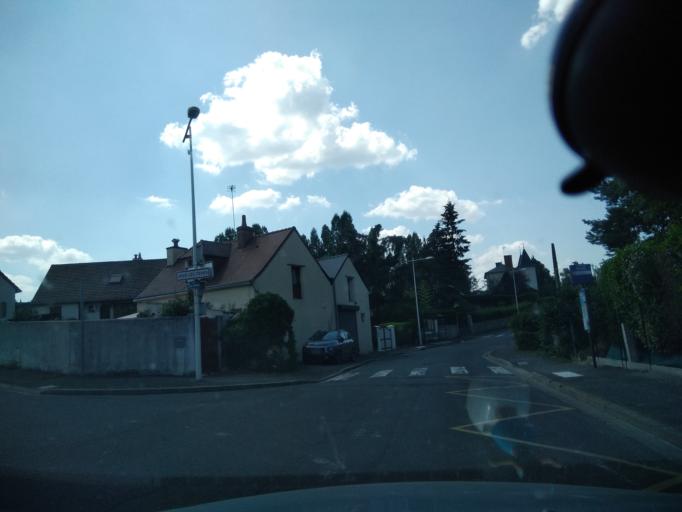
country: FR
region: Centre
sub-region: Departement d'Indre-et-Loire
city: Joue-les-Tours
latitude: 47.3458
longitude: 0.6842
